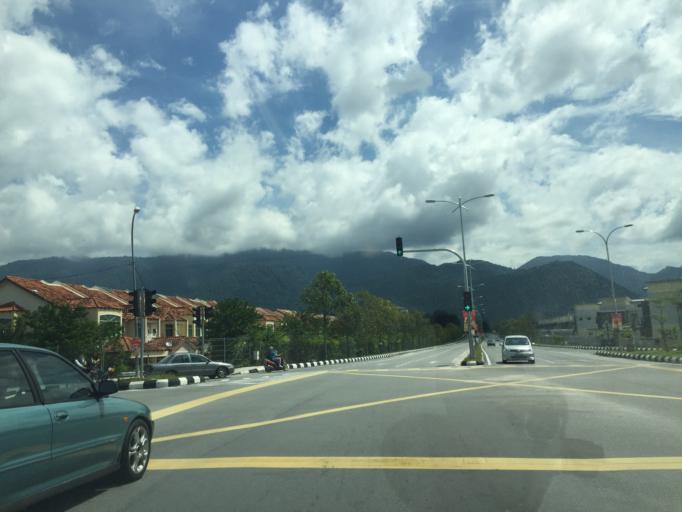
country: MY
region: Perak
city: Kampar
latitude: 4.3281
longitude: 101.1332
